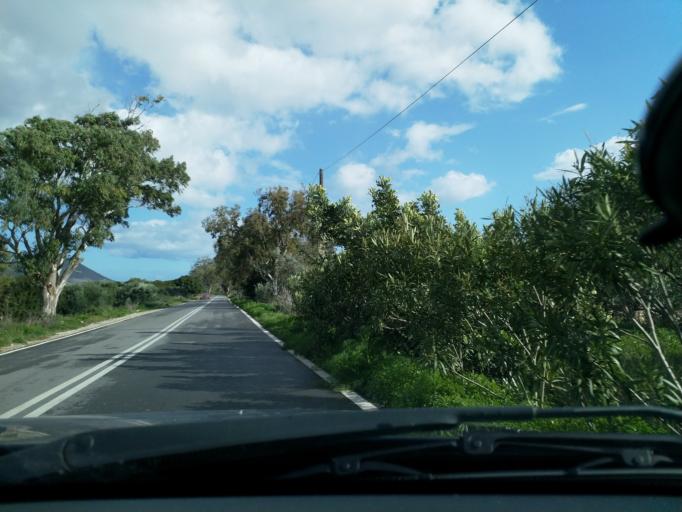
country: GR
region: Crete
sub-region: Nomos Chanias
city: Mouzouras
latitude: 35.5176
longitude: 24.1365
